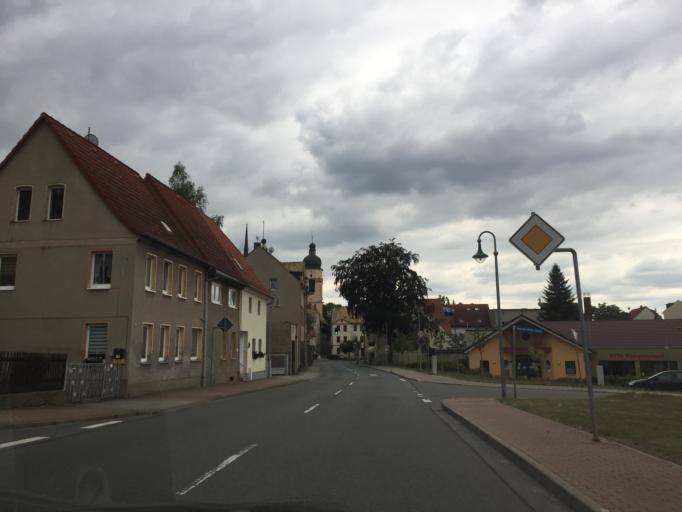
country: DE
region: Thuringia
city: Gossnitz
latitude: 50.8898
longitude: 12.4337
